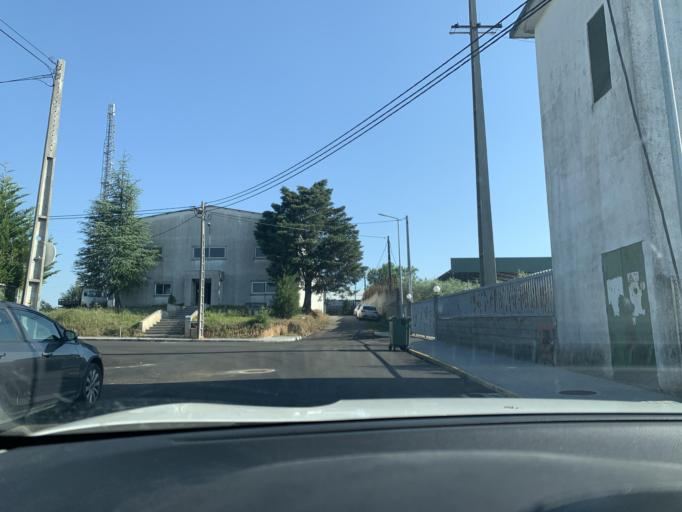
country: PT
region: Viseu
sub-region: Concelho de Tondela
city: Tondela
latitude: 40.4855
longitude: -8.0912
